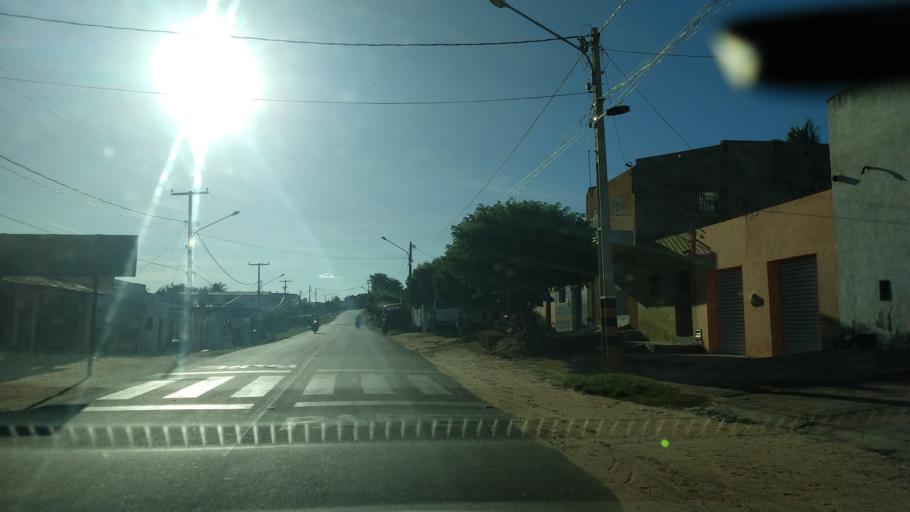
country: BR
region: Rio Grande do Norte
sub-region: Sao Jose Do Campestre
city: Sao Jose do Campestre
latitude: -6.3142
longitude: -35.7131
